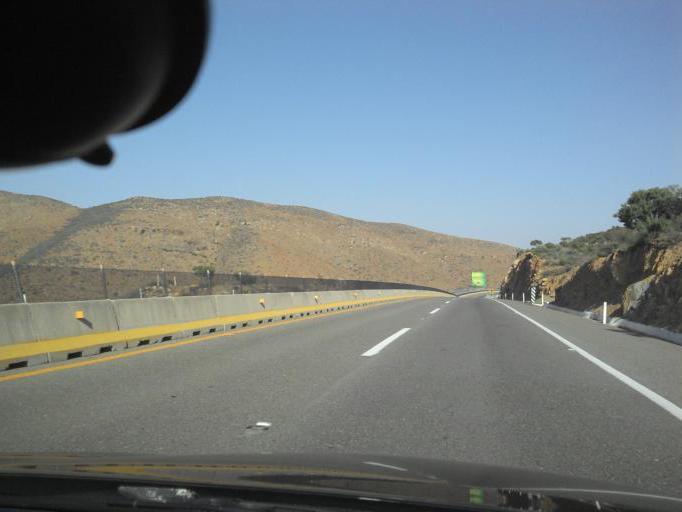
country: MX
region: Baja California
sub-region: Tijuana
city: El Nino
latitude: 32.5574
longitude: -116.8103
